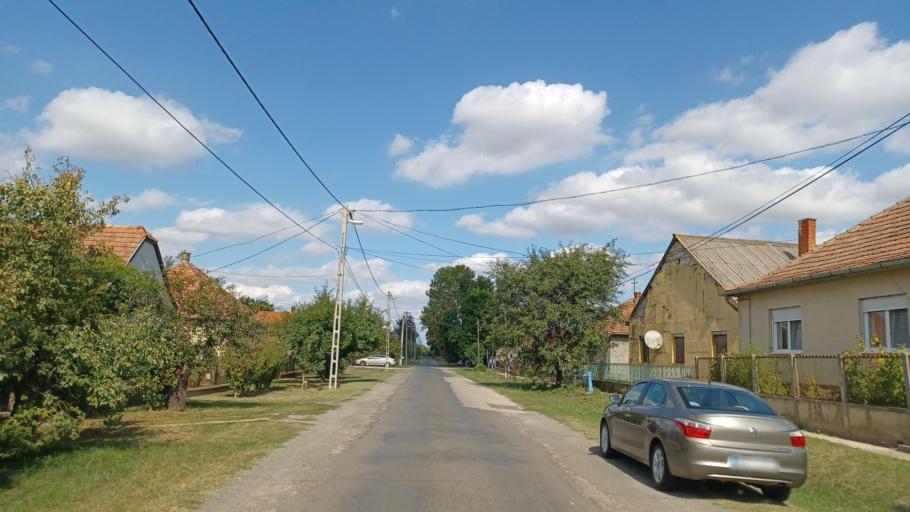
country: HU
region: Tolna
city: Pincehely
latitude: 46.7227
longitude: 18.4747
